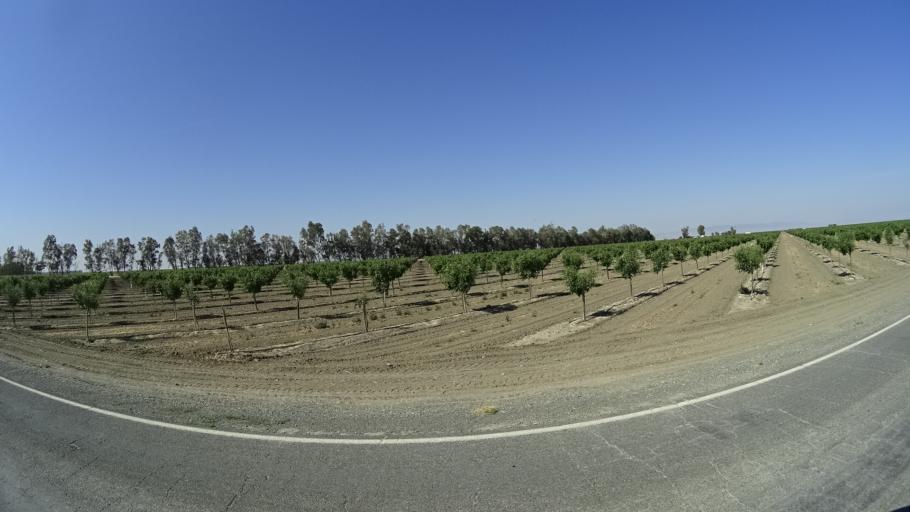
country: US
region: California
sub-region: Fresno County
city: Riverdale
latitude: 36.3808
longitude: -119.9343
